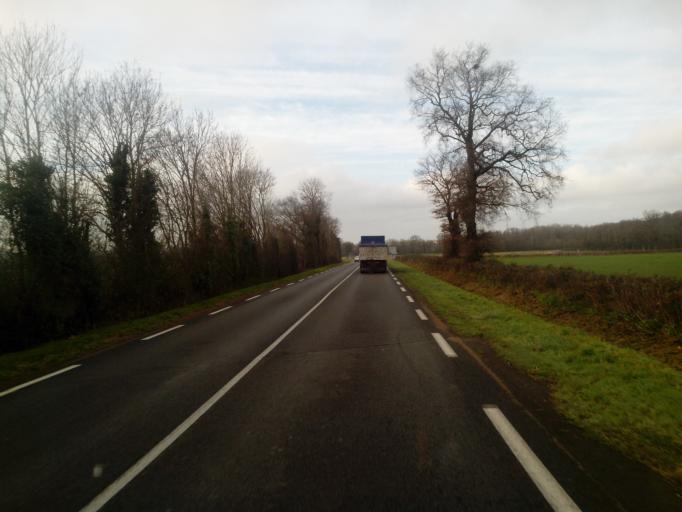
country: FR
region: Poitou-Charentes
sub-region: Departement des Deux-Sevres
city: Chiche
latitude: 46.7768
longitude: -0.3276
